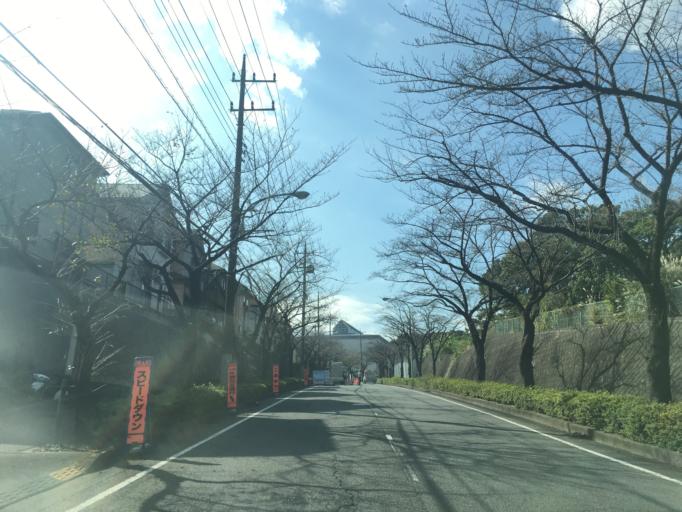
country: JP
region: Tokyo
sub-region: Machida-shi
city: Machida
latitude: 35.5881
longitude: 139.4154
